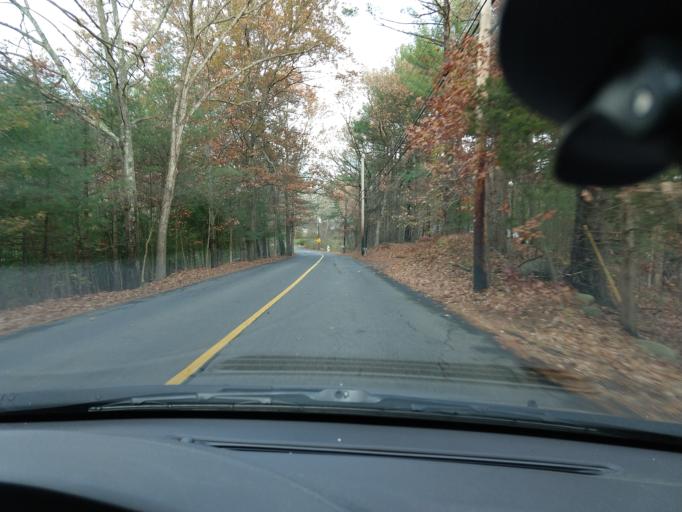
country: US
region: Massachusetts
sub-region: Middlesex County
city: West Concord
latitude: 42.4808
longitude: -71.3820
